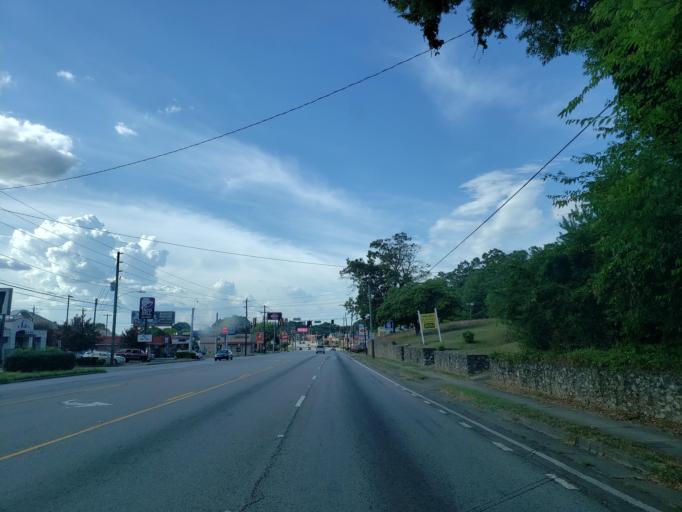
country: US
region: Georgia
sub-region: Floyd County
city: Rome
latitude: 34.2424
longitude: -85.1611
